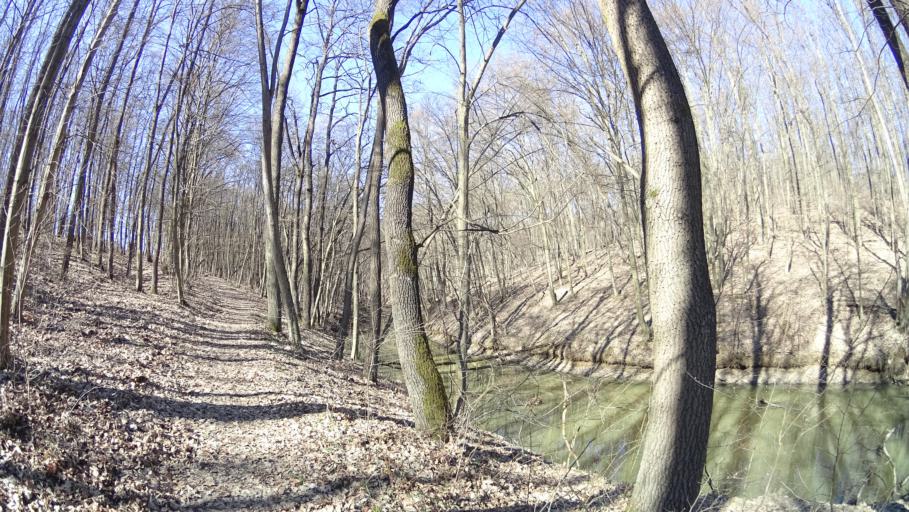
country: HU
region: Pest
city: Veroce
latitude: 47.8607
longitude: 19.0881
